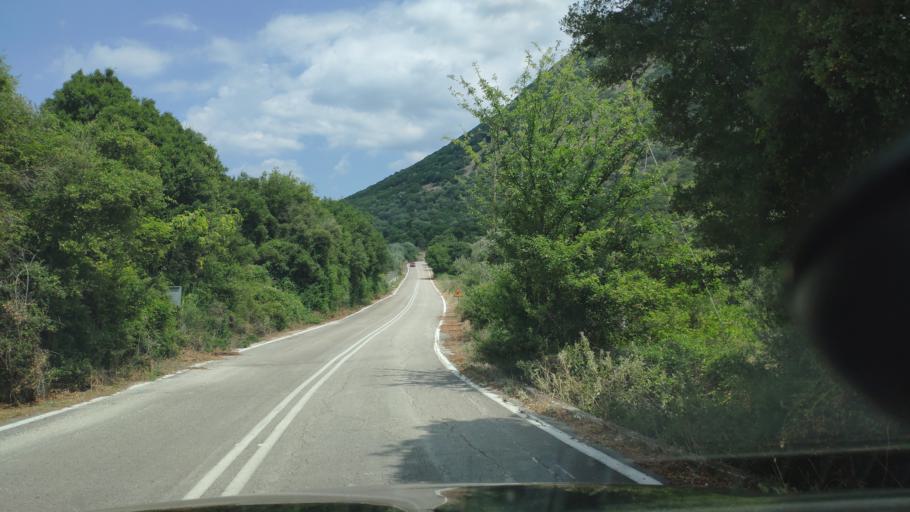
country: GR
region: Epirus
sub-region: Nomos Artas
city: Kampi
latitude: 39.2714
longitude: 20.9299
